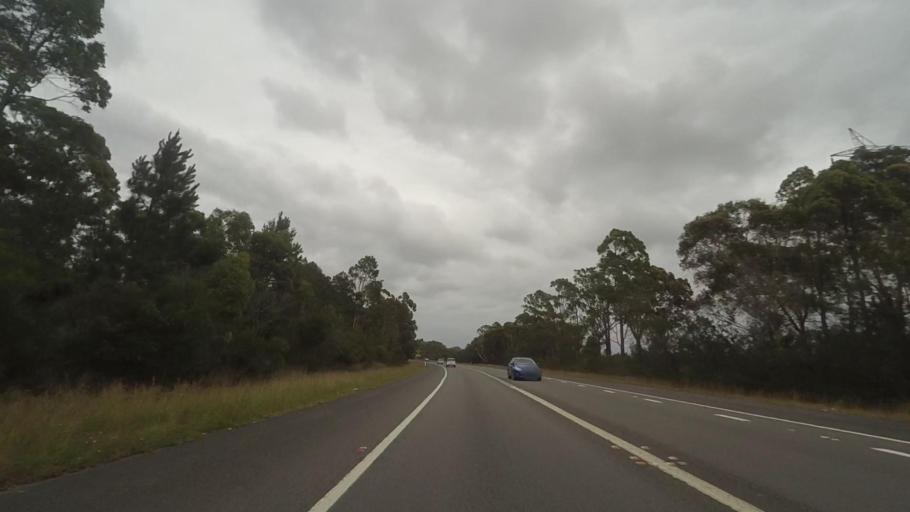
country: AU
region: New South Wales
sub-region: Wyong Shire
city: Charmhaven
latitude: -33.2049
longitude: 151.5055
